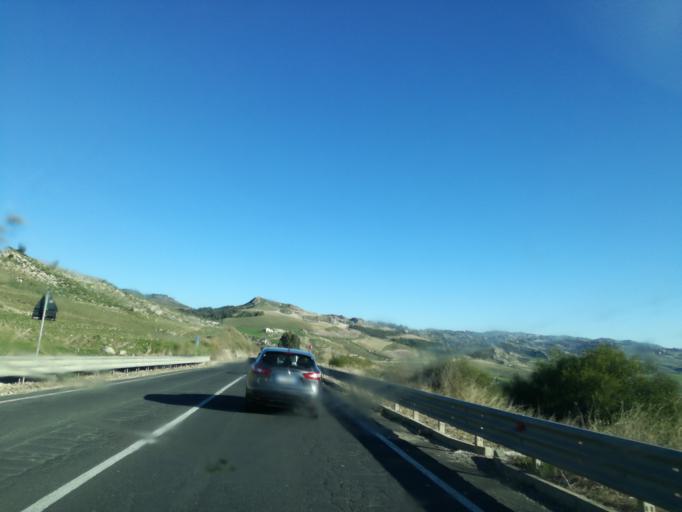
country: IT
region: Sicily
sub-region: Catania
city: San Michele di Ganzaria
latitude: 37.2327
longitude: 14.4481
